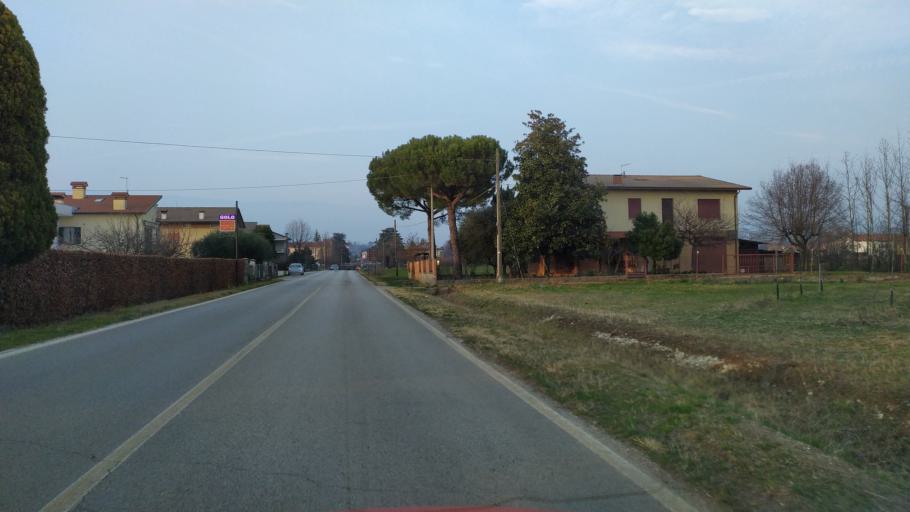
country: IT
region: Veneto
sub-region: Provincia di Vicenza
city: Sarcedo
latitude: 45.6902
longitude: 11.5315
